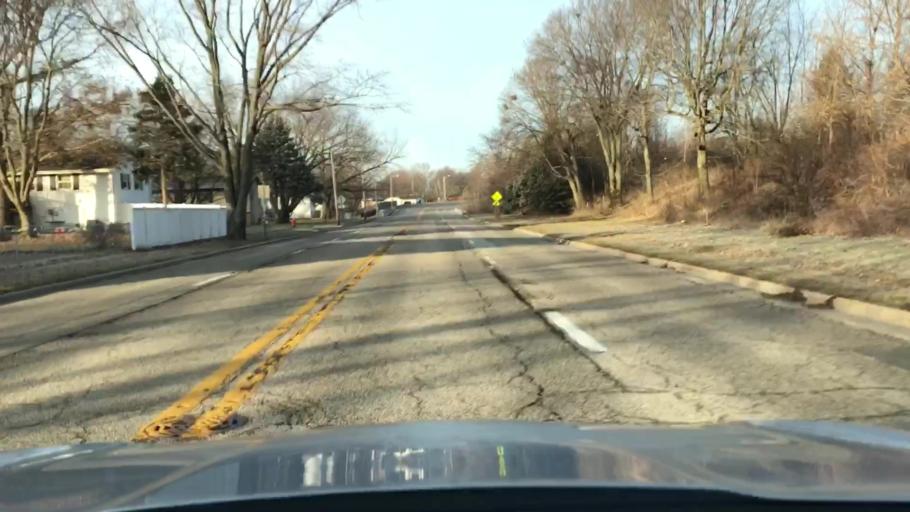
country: US
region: Illinois
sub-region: McLean County
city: Normal
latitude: 40.5027
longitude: -88.9602
